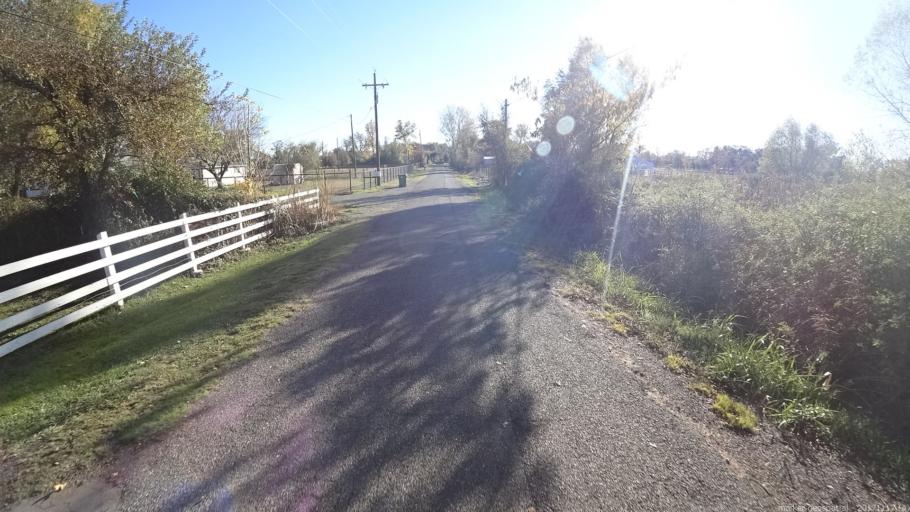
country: US
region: California
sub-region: Shasta County
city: Cottonwood
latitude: 40.3968
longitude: -122.2168
